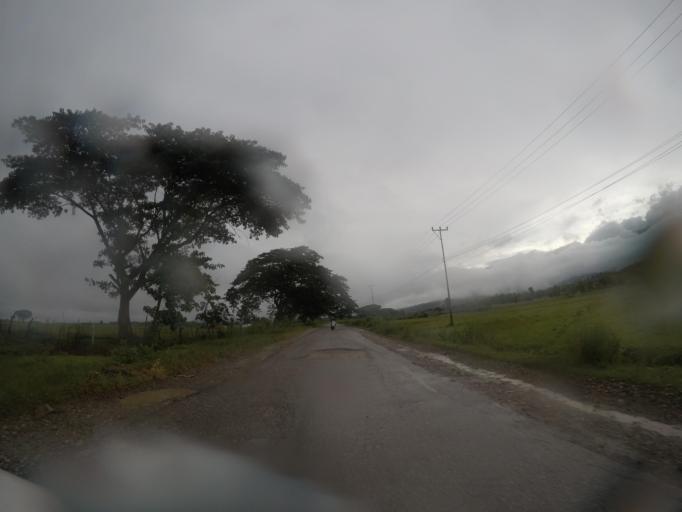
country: TL
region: Bobonaro
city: Maliana
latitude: -8.9910
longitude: 125.1808
